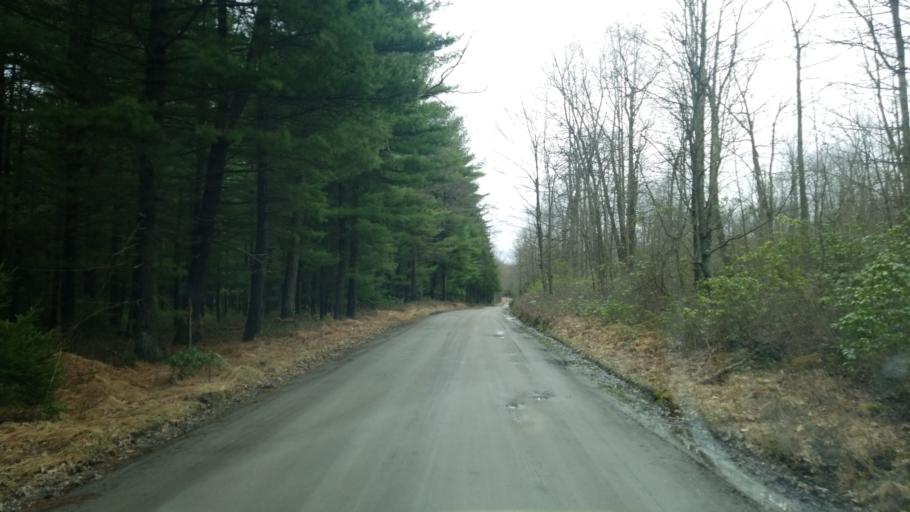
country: US
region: Pennsylvania
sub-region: Clearfield County
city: Shiloh
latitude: 41.1681
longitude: -78.2573
